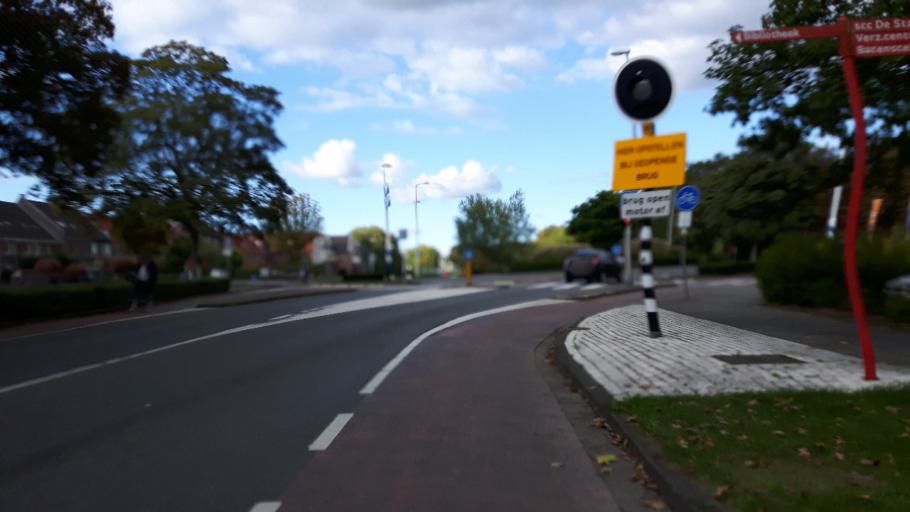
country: NL
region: Utrecht
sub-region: Gemeente Vianen
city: Vianen
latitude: 51.9924
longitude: 5.0963
